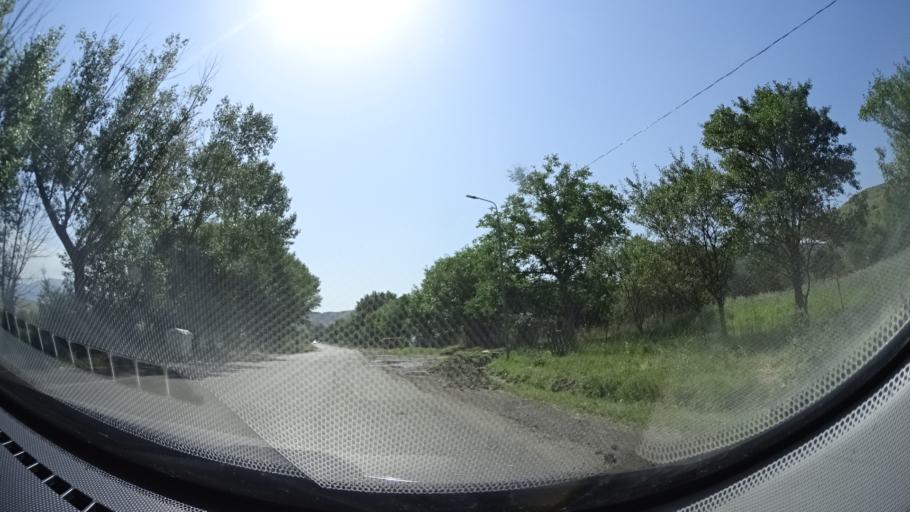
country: GE
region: Samtskhe-Javakheti
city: Akhaltsikhe
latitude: 41.6382
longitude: 43.0340
